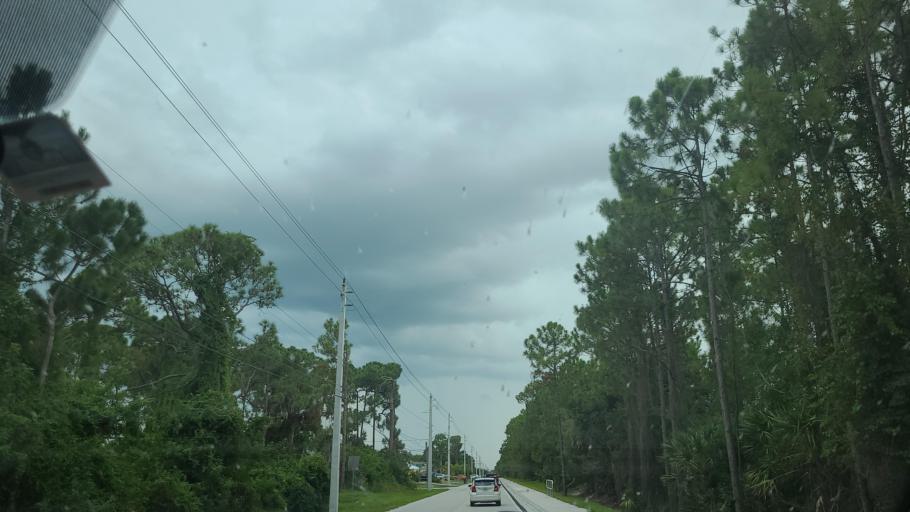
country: US
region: Florida
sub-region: Saint Lucie County
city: Port Saint Lucie
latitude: 27.2297
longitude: -80.3997
